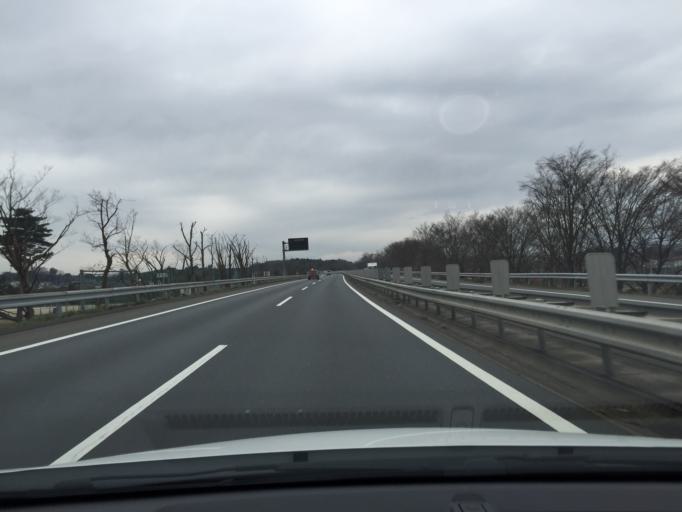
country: JP
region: Saitama
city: Sayama
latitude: 35.8814
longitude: 139.3831
